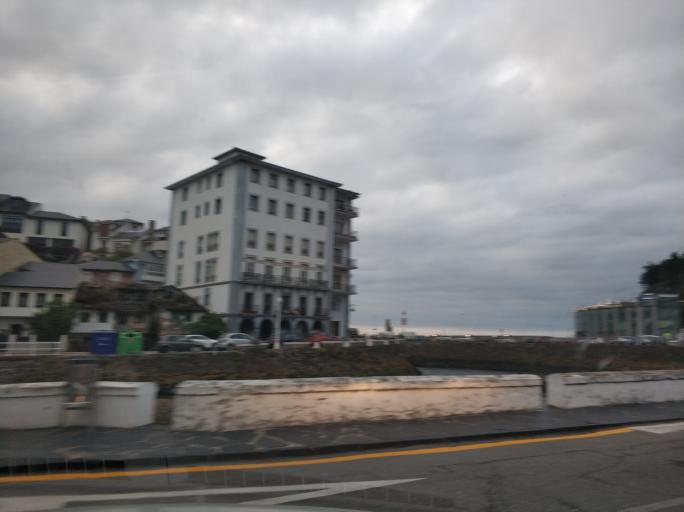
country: ES
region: Asturias
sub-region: Province of Asturias
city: Navia
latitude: 43.5452
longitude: -6.5342
